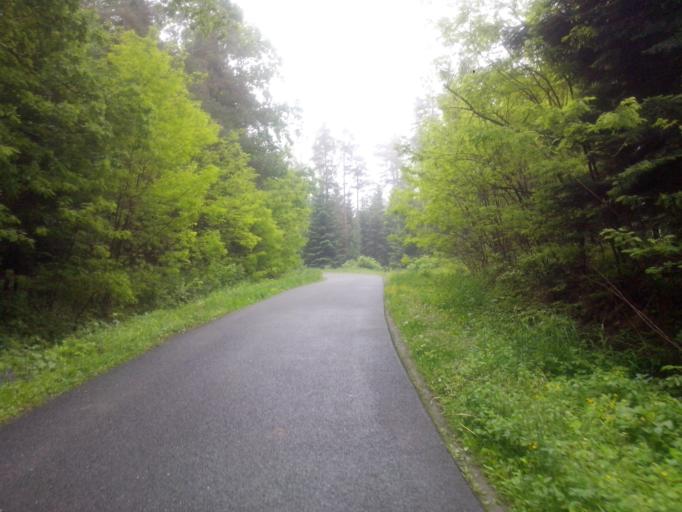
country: PL
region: Subcarpathian Voivodeship
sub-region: Powiat strzyzowski
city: Wysoka Strzyzowska
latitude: 49.8250
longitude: 21.7826
